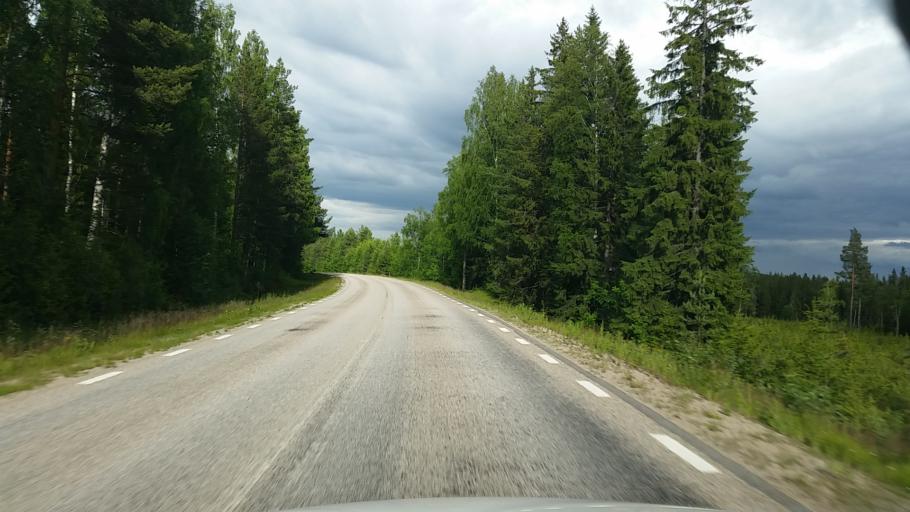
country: SE
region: Gaevleborg
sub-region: Ljusdals Kommun
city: Farila
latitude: 61.9786
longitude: 15.1182
